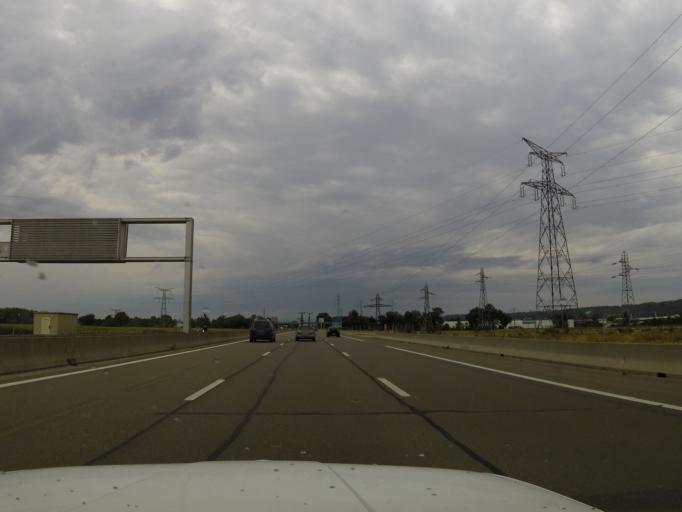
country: FR
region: Rhone-Alpes
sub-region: Departement de l'Ain
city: Beynost
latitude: 45.8245
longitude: 5.0057
